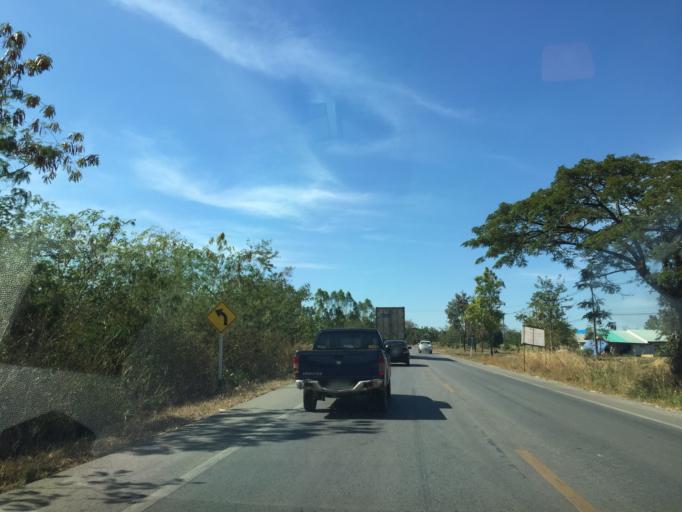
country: TH
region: Changwat Nong Bua Lamphu
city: Na Klang
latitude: 17.3180
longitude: 102.1553
